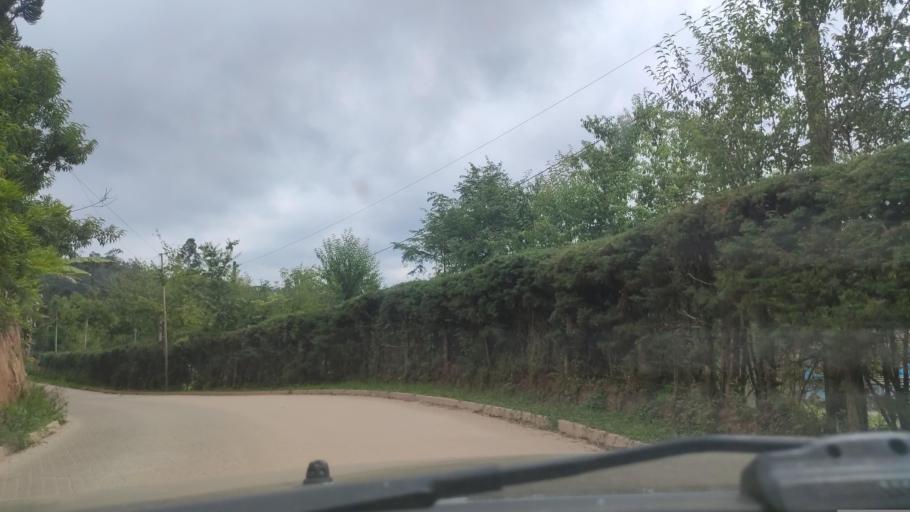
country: BR
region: Minas Gerais
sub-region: Paraisopolis
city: Paraisopolis
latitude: -22.6750
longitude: -45.8552
